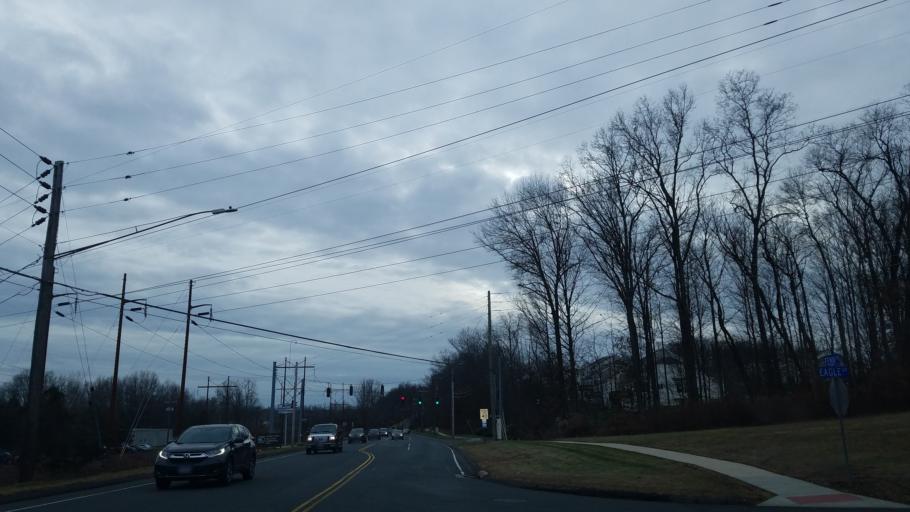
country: US
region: Connecticut
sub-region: Hartford County
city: Newington
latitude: 41.7106
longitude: -72.7467
